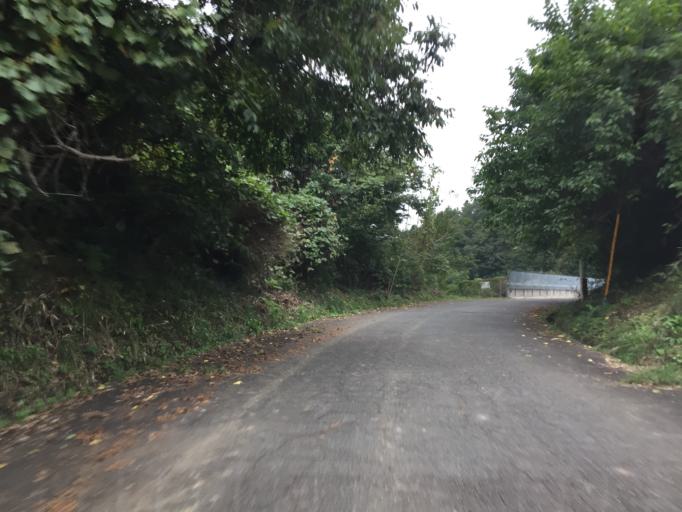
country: JP
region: Fukushima
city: Fukushima-shi
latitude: 37.6740
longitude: 140.4497
